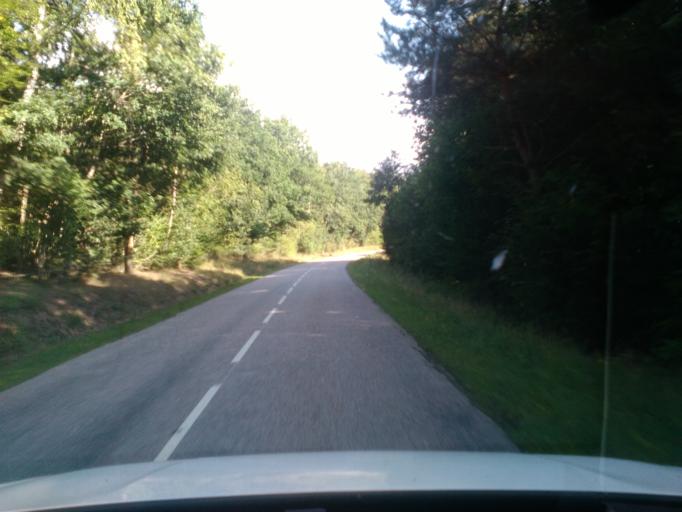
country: FR
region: Lorraine
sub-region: Departement des Vosges
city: Taintrux
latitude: 48.2348
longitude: 6.9019
